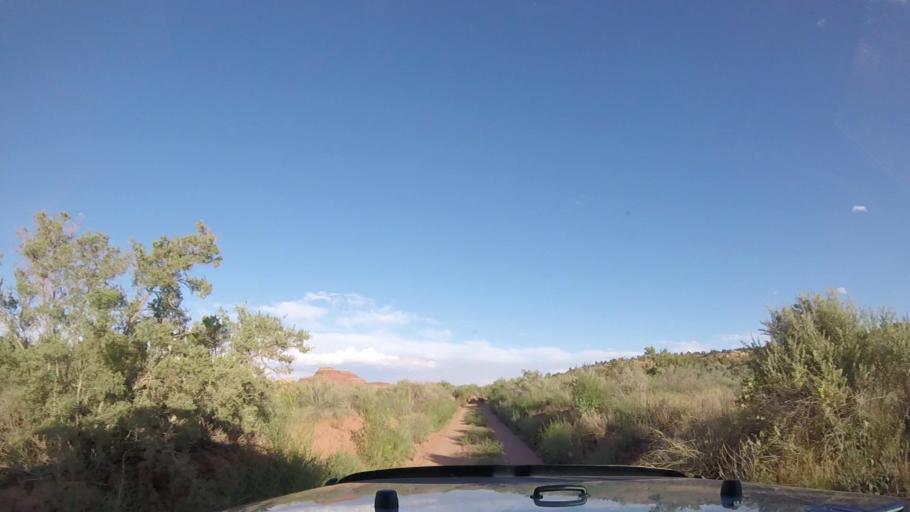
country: US
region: Utah
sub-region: Grand County
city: Moab
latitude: 38.1918
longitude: -109.7805
